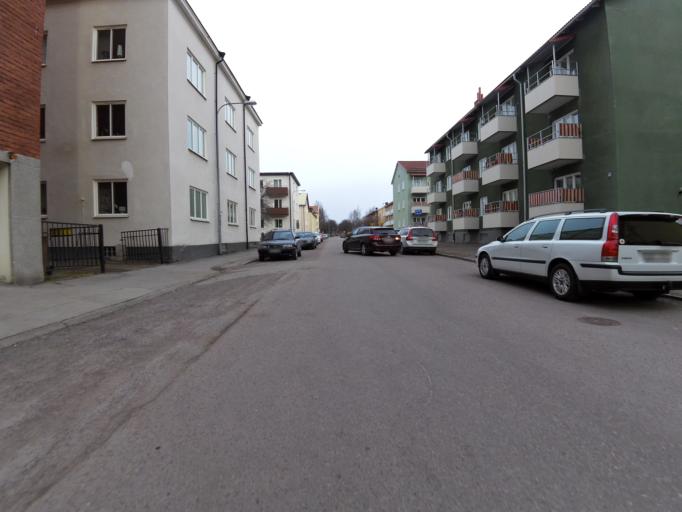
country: SE
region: Gaevleborg
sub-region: Gavle Kommun
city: Gavle
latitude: 60.6757
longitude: 17.1339
